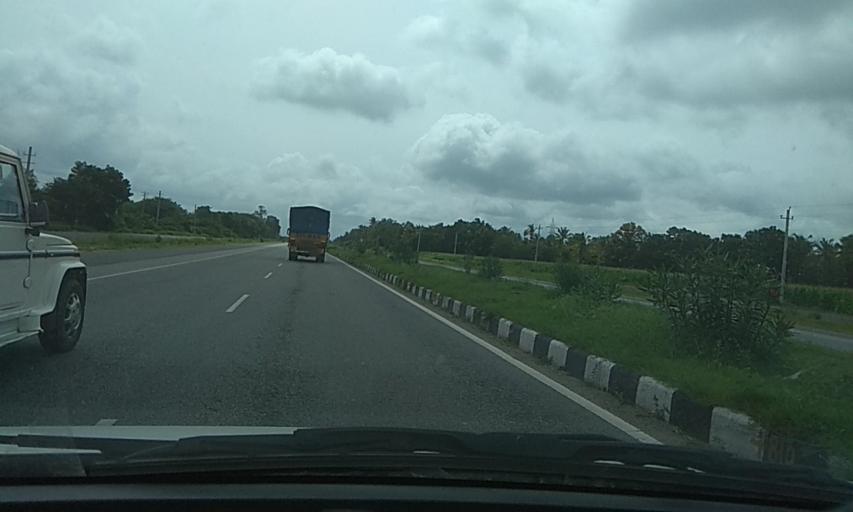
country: IN
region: Karnataka
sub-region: Davanagere
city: Mayakonda
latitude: 14.4025
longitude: 76.0078
